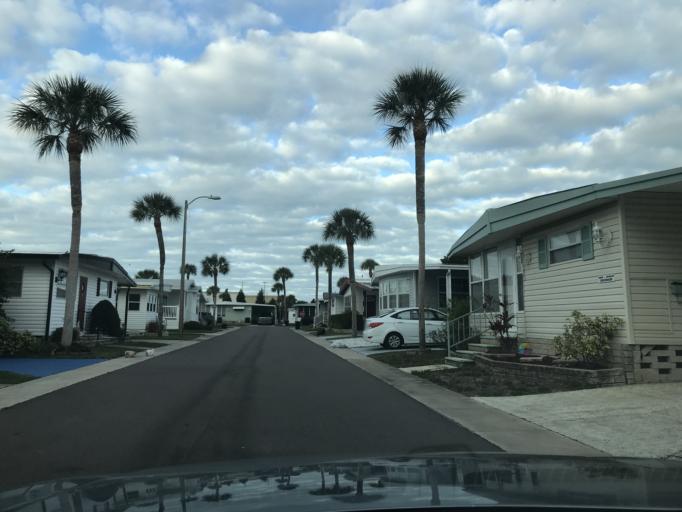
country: US
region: Florida
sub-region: Pinellas County
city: Largo
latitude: 27.9269
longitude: -82.7836
